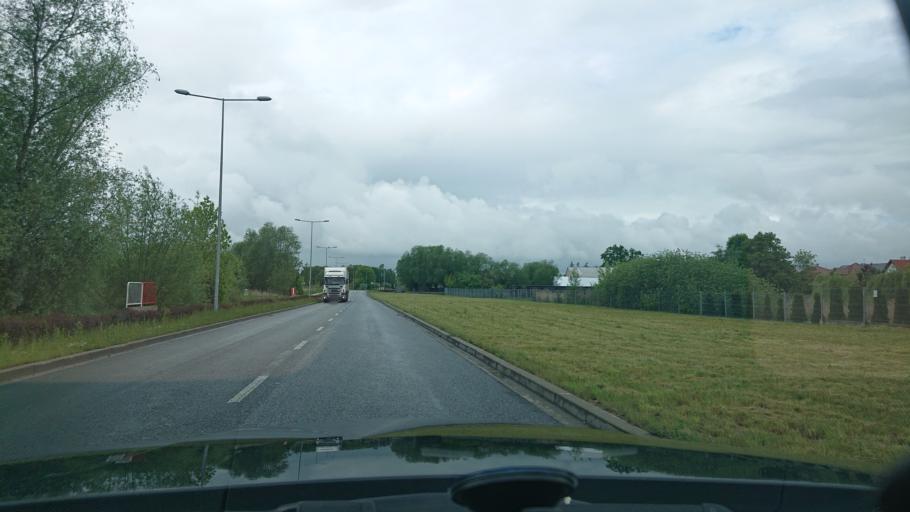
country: PL
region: Greater Poland Voivodeship
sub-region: Powiat gnieznienski
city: Gniezno
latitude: 52.5208
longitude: 17.6181
